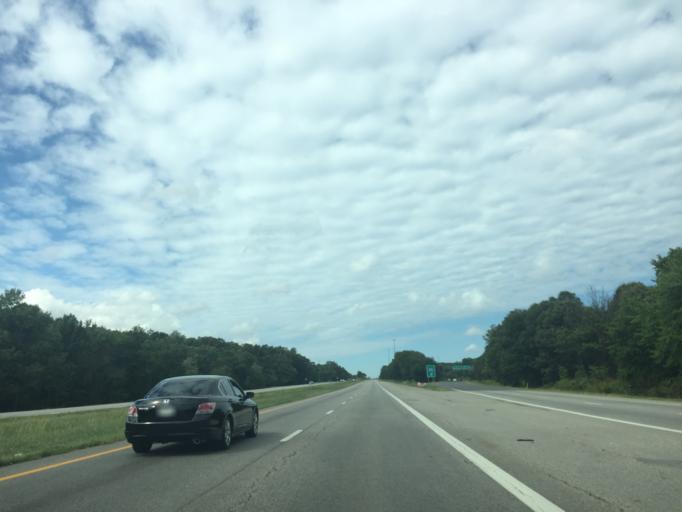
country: US
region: Maryland
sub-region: Prince George's County
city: West Laurel
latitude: 39.1022
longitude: -76.8764
